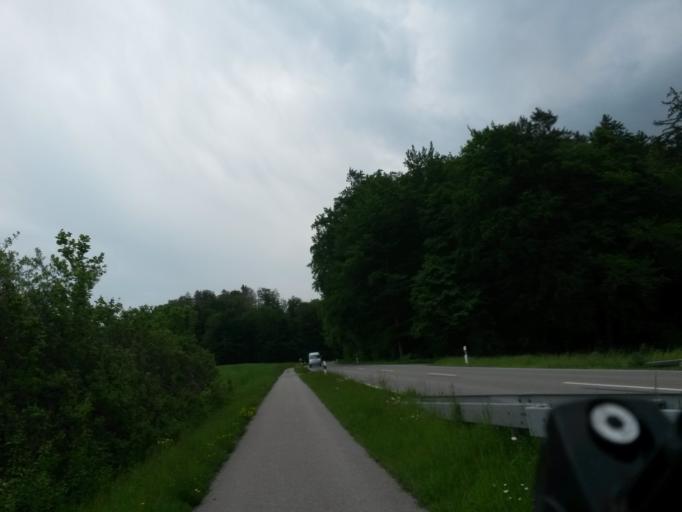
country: DE
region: Baden-Wuerttemberg
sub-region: Tuebingen Region
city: Bad Waldsee
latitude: 47.9235
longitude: 9.7729
